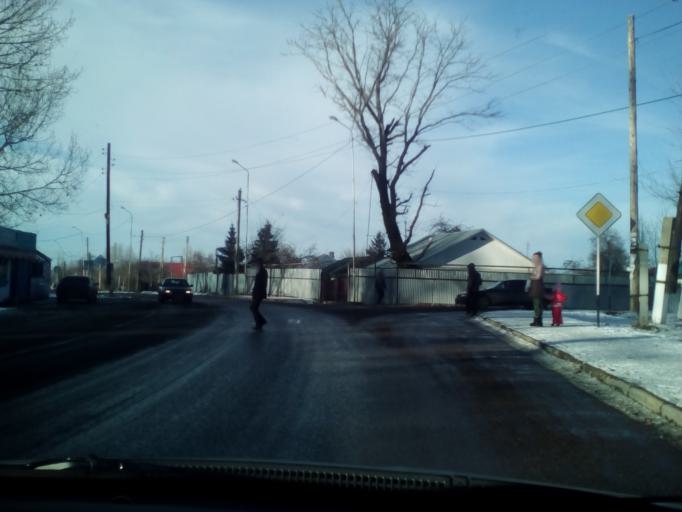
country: KZ
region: Almaty Oblysy
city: Burunday
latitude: 43.1587
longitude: 76.4184
